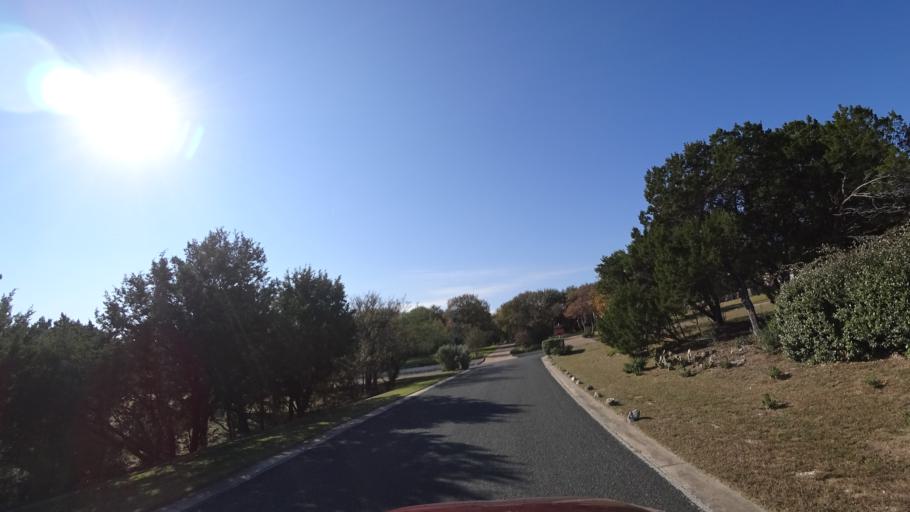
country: US
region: Texas
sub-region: Williamson County
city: Anderson Mill
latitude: 30.3825
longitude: -97.8280
